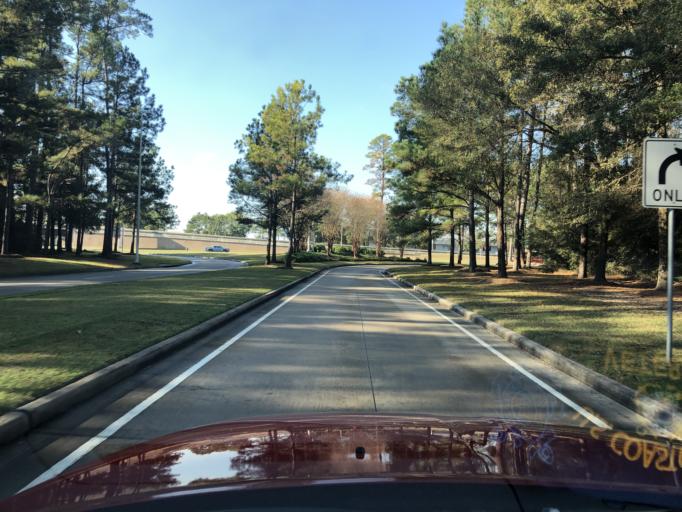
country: US
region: Texas
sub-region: Harris County
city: Aldine
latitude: 29.9721
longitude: -95.3384
